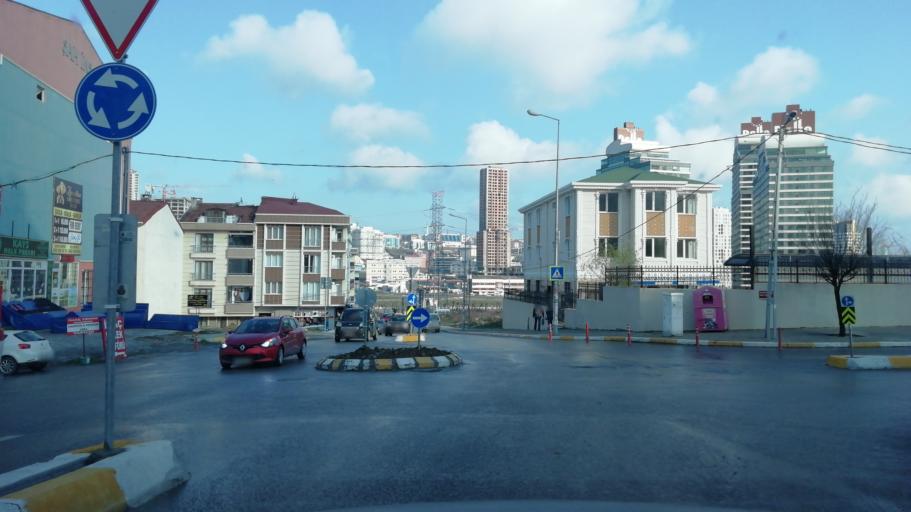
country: TR
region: Istanbul
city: Esenyurt
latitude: 41.0122
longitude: 28.6724
